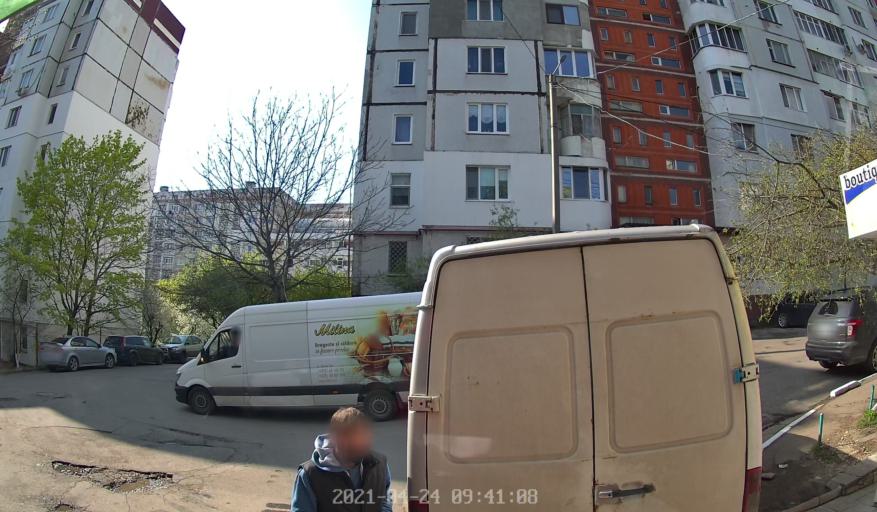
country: NG
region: Niger
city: Lemu
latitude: 9.4087
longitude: 5.7792
